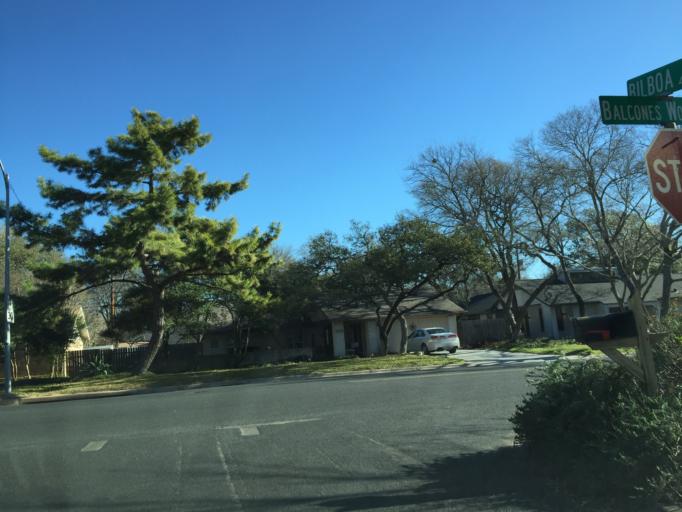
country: US
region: Texas
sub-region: Williamson County
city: Jollyville
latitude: 30.4056
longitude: -97.7392
